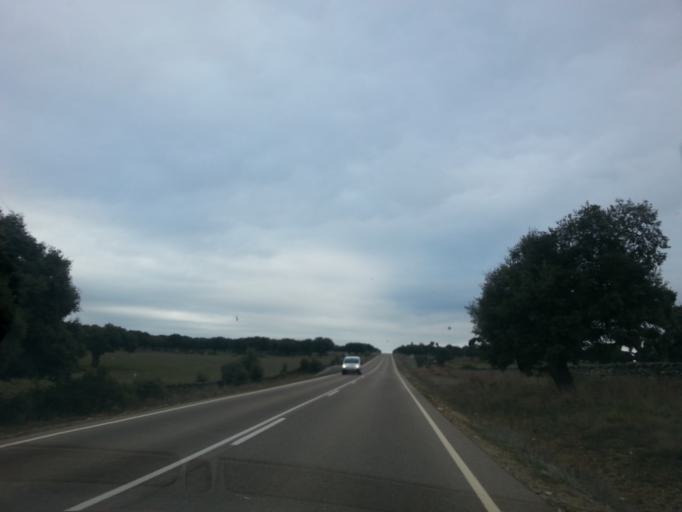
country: ES
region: Castille and Leon
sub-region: Provincia de Salamanca
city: Vecinos
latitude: 40.7596
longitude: -5.8992
